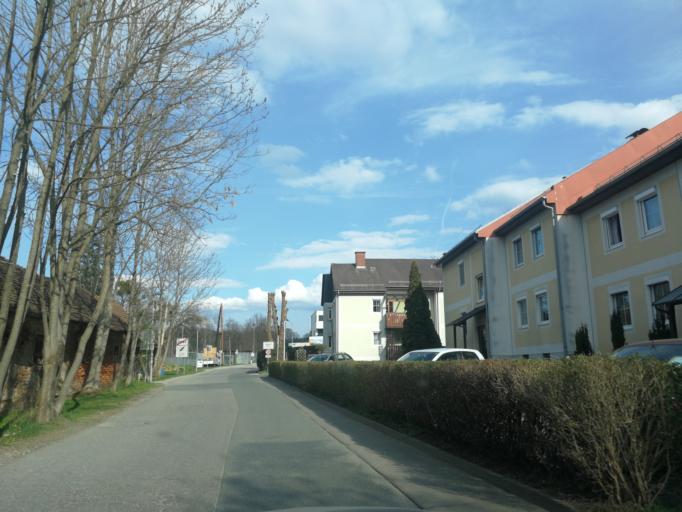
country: AT
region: Styria
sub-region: Graz Stadt
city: Mariatrost
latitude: 47.0734
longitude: 15.5079
